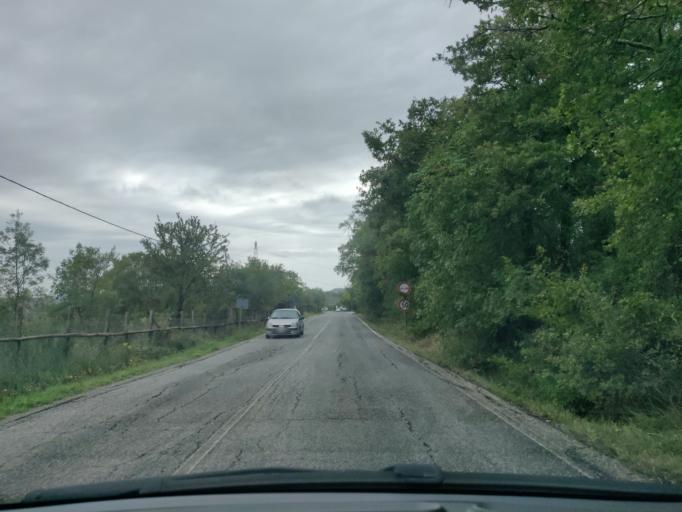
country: IT
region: Latium
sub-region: Citta metropolitana di Roma Capitale
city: Allumiere
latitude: 42.1273
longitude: 11.8654
